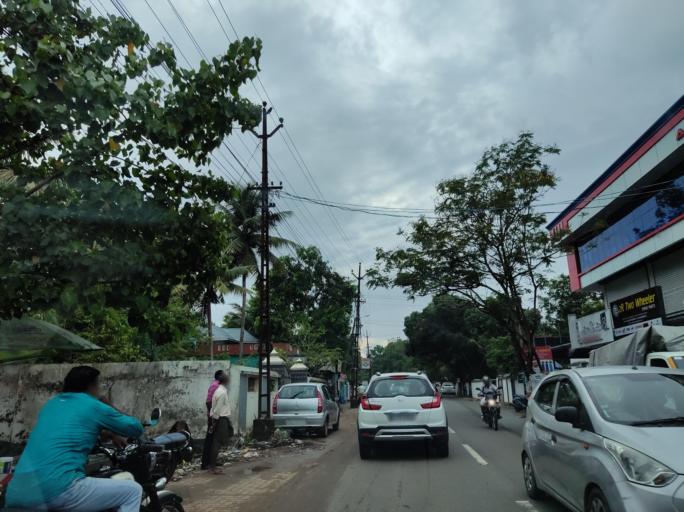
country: IN
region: Kerala
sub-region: Alappuzha
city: Mavelikara
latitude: 9.2501
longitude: 76.4918
